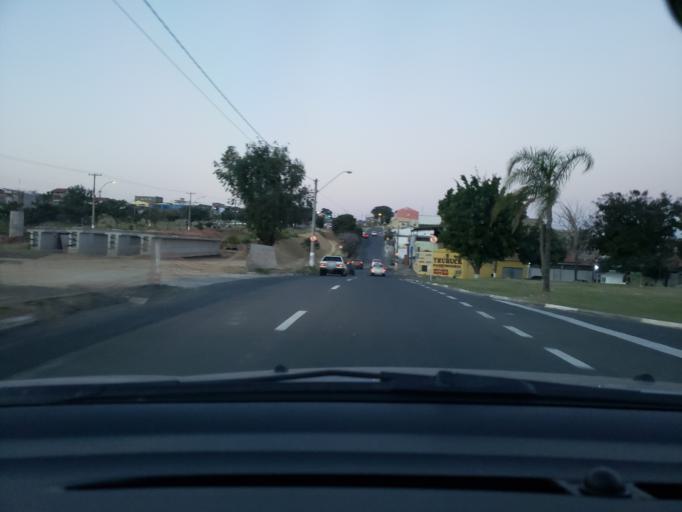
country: BR
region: Sao Paulo
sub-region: Campinas
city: Campinas
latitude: -22.9222
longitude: -47.1177
